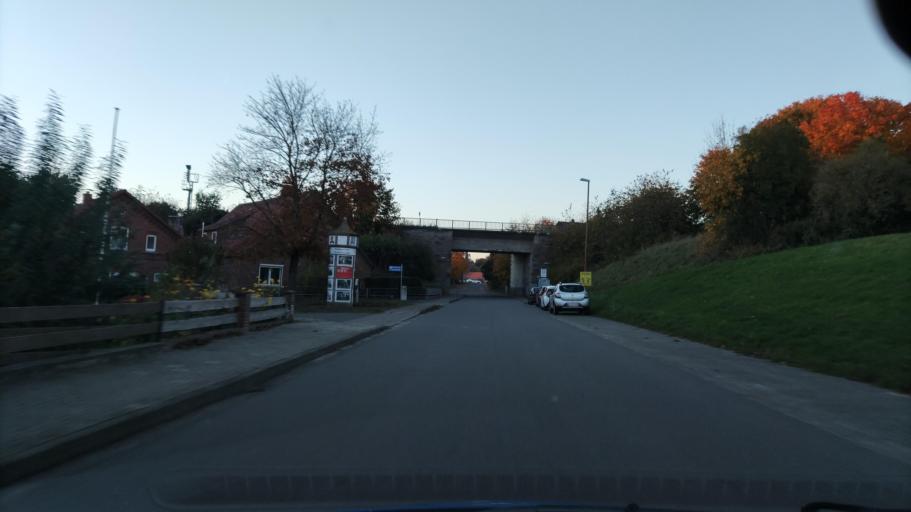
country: DE
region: Schleswig-Holstein
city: Lauenburg
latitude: 53.3647
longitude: 10.5599
